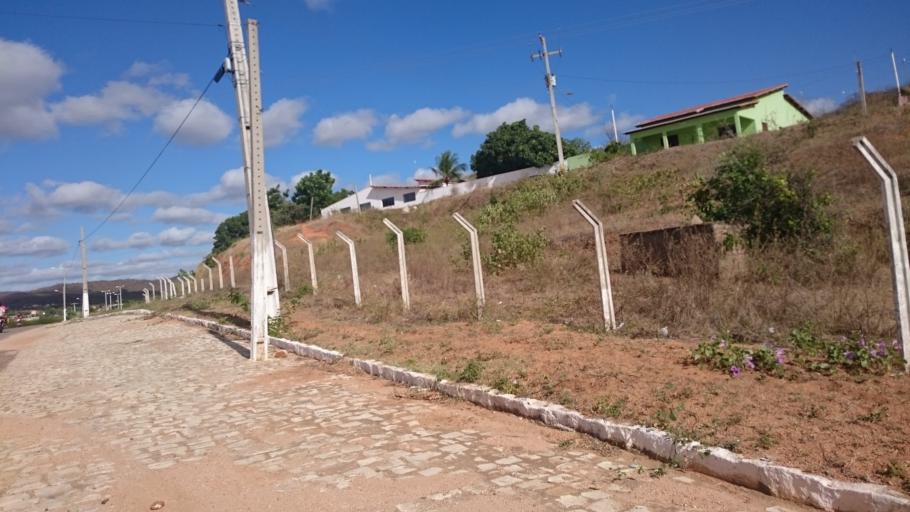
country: BR
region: Paraiba
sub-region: Catole Do Rocha
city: Sao Bento
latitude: -6.1532
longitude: -37.7609
